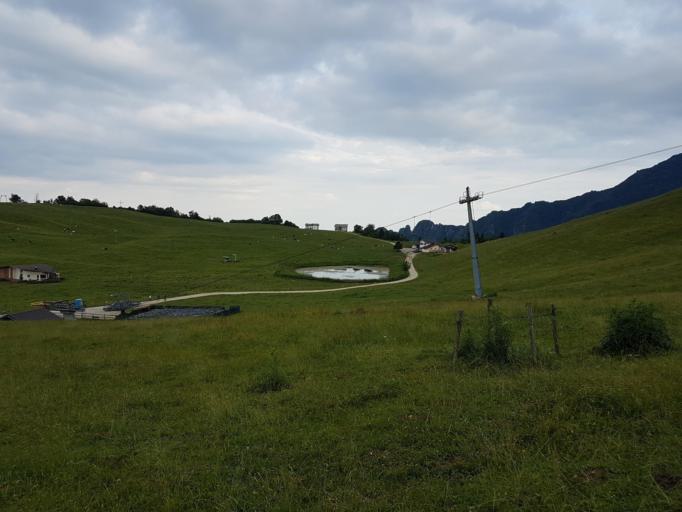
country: IT
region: Veneto
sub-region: Provincia di Vicenza
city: Recoaro Terme
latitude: 45.6781
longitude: 11.2183
